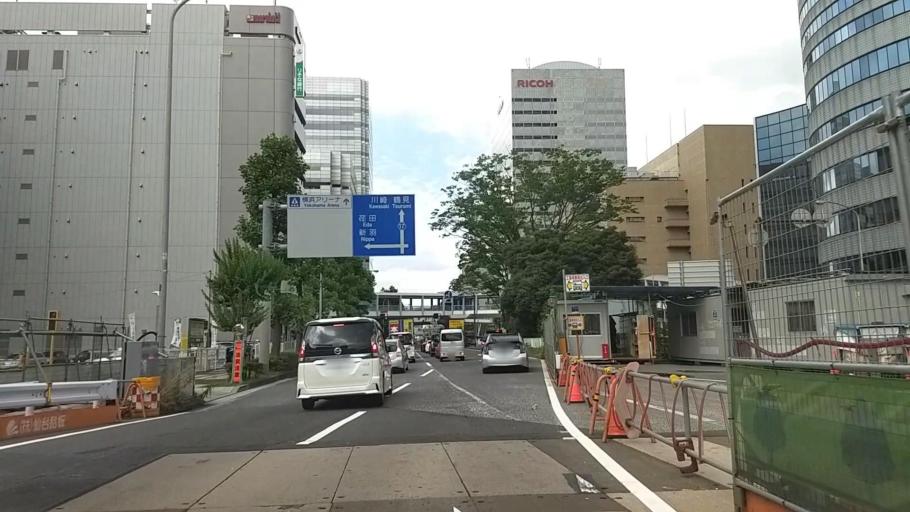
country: JP
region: Kanagawa
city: Yokohama
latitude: 35.5101
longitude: 139.6186
